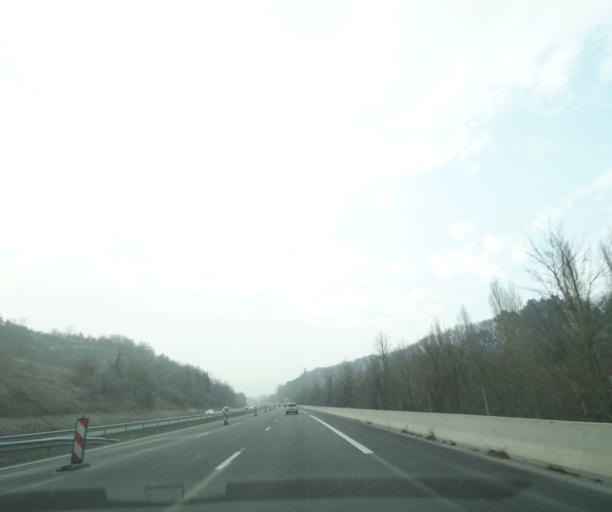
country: FR
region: Rhone-Alpes
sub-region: Departement du Rhone
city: Lissieu
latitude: 45.8569
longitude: 4.7420
